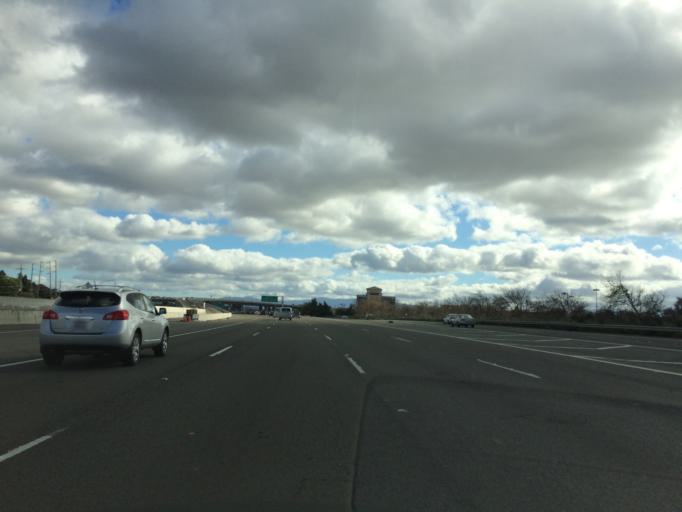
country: US
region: California
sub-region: Santa Clara County
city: Milpitas
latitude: 37.4323
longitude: -121.9191
